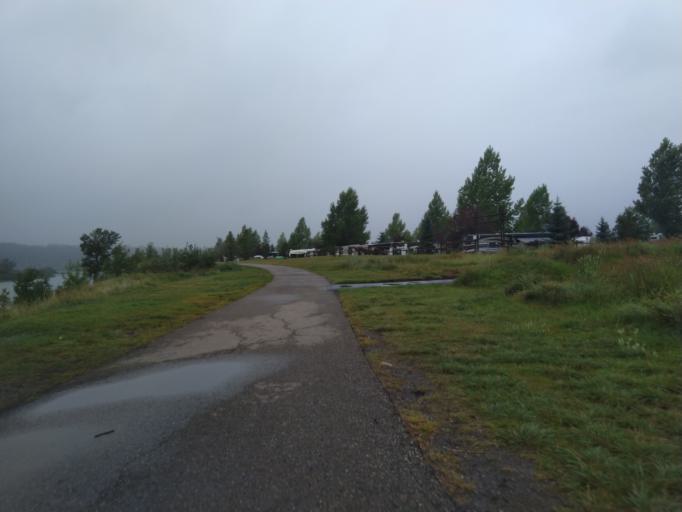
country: CA
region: Alberta
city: Cochrane
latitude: 51.1741
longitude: -114.4547
